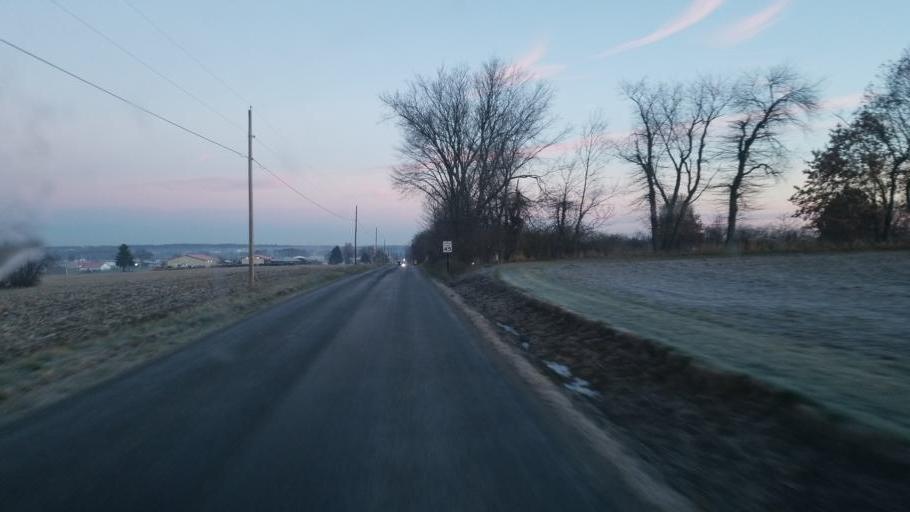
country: US
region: Ohio
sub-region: Wayne County
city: Orrville
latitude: 40.7888
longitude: -81.7752
